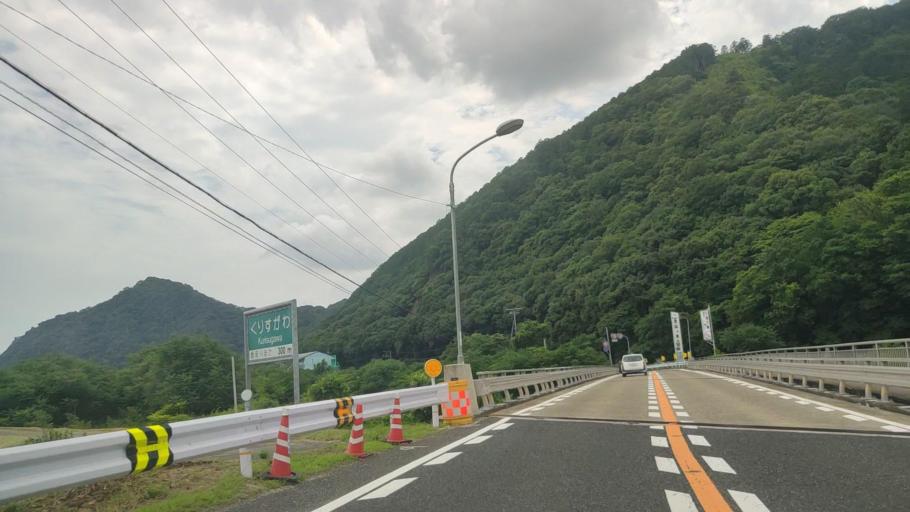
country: JP
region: Hyogo
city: Tatsunocho-tominaga
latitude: 34.8838
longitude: 134.5470
